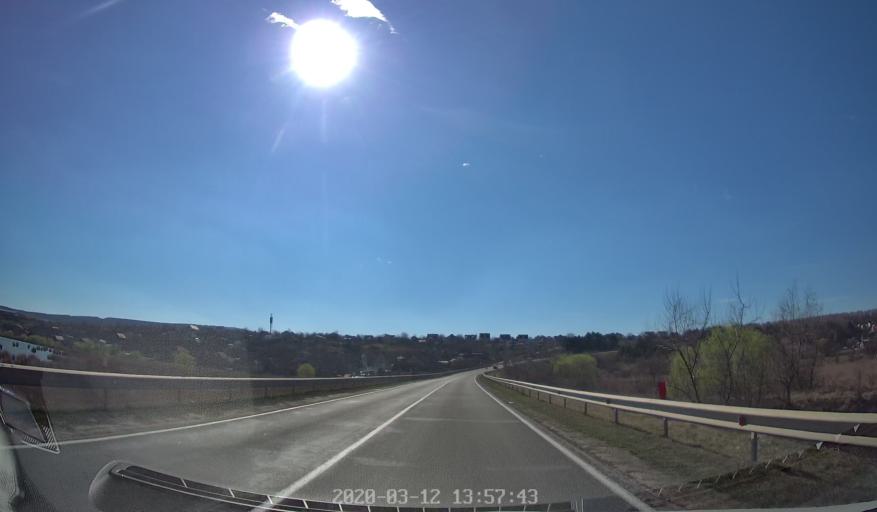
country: MD
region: Chisinau
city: Vatra
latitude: 46.9898
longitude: 28.6851
